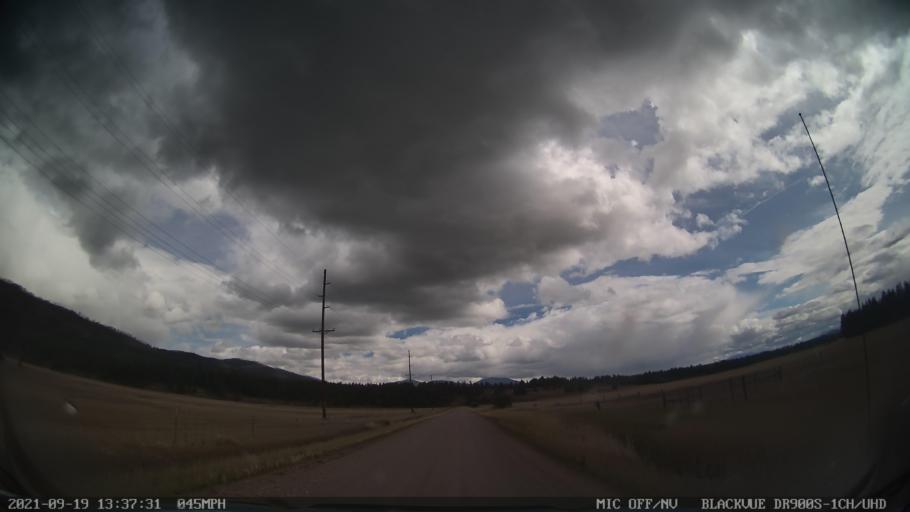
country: US
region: Montana
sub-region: Missoula County
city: Seeley Lake
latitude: 47.1067
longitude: -113.2819
